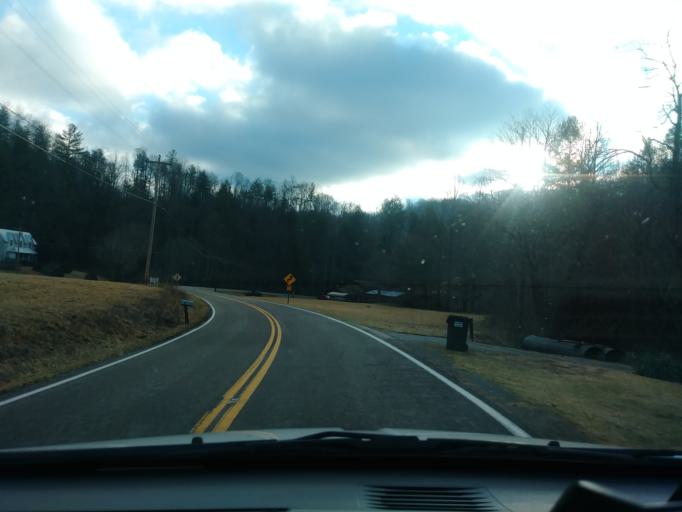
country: US
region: Tennessee
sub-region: Carter County
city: Elizabethton
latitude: 36.2164
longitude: -82.2054
